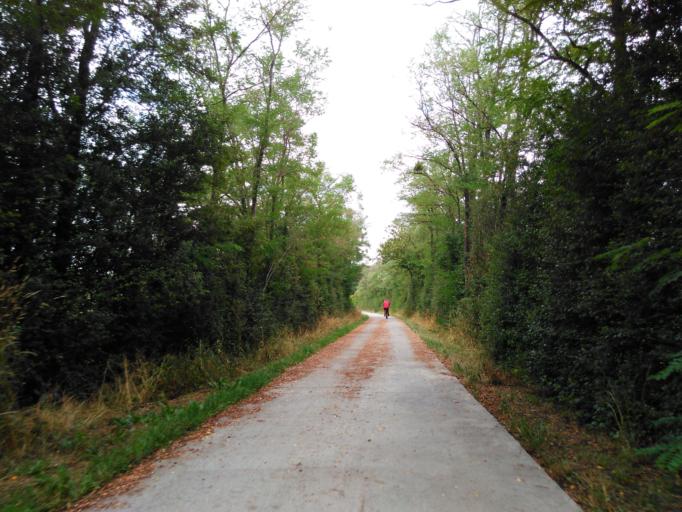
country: LU
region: Grevenmacher
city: Gonderange
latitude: 49.6839
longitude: 6.2501
